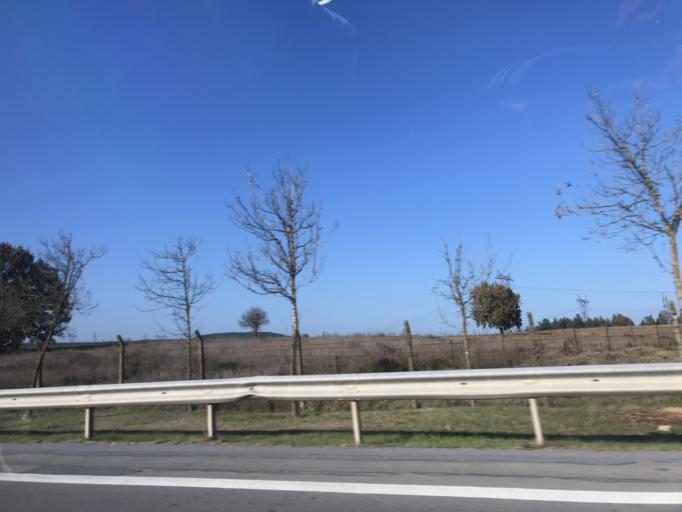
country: TR
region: Istanbul
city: Sultanbeyli
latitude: 40.9340
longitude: 29.3471
